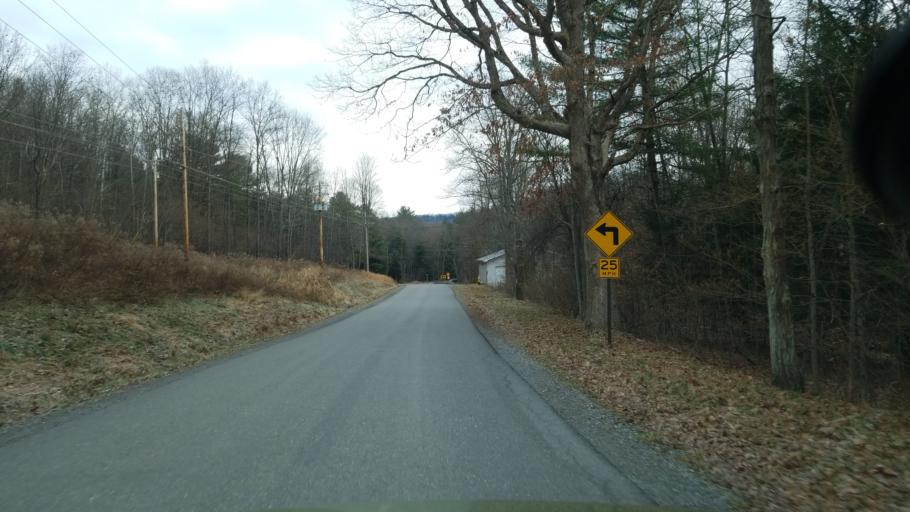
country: US
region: Pennsylvania
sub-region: Clearfield County
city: Treasure Lake
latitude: 41.1026
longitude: -78.6755
